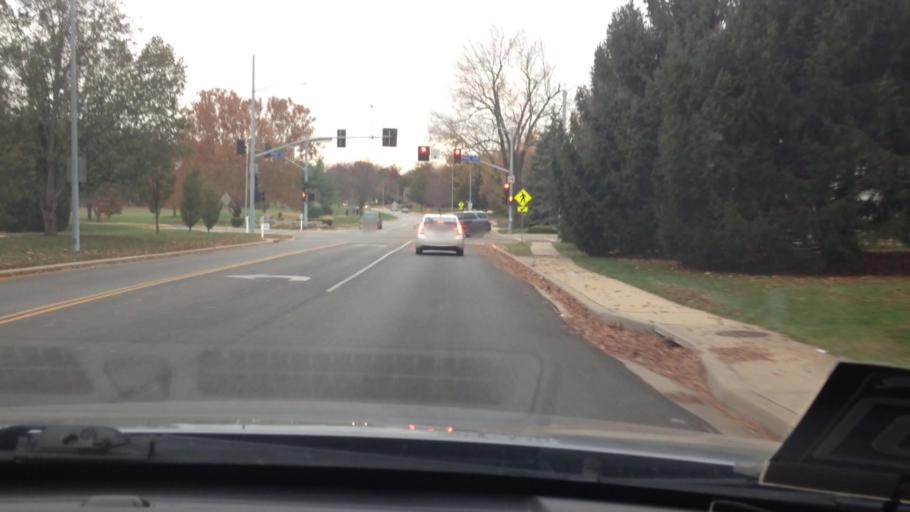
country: US
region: Kansas
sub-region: Johnson County
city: Prairie Village
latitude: 38.9735
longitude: -94.6371
